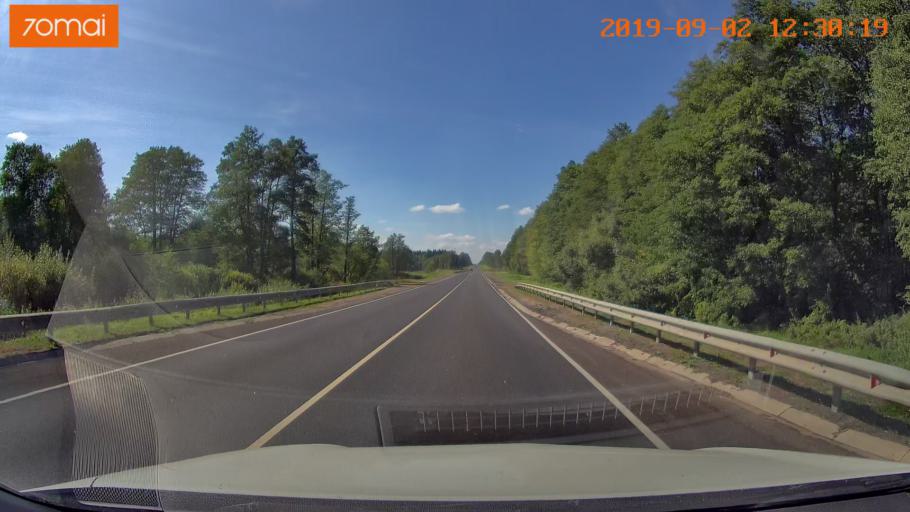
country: RU
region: Smolensk
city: Shumyachi
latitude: 53.8330
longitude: 32.4775
